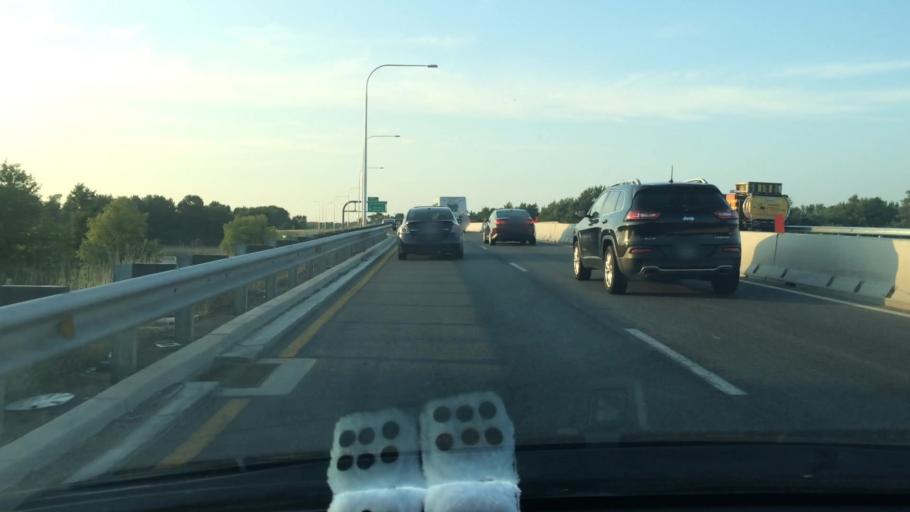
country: US
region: Delaware
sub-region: New Castle County
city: Newport
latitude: 39.6989
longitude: -75.6011
